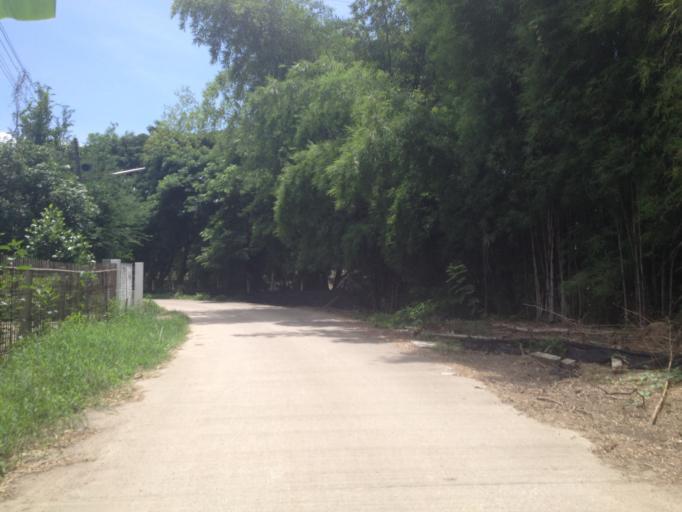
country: TH
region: Chiang Mai
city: Hang Dong
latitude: 18.7532
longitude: 98.9285
